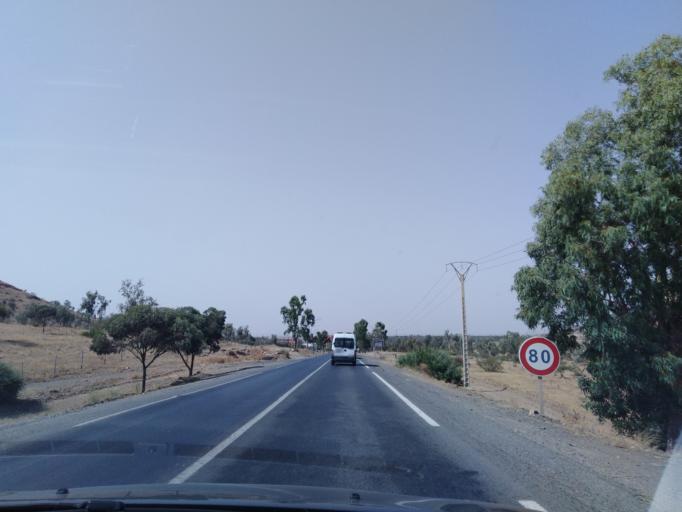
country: MA
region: Marrakech-Tensift-Al Haouz
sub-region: Kelaa-Des-Sraghna
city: Sidi Bou Othmane
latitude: 31.8859
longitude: -7.9450
